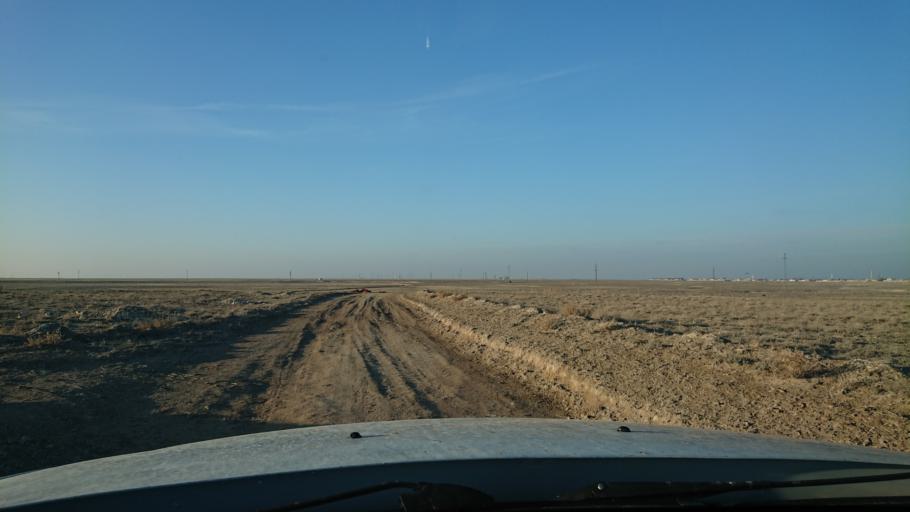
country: TR
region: Aksaray
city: Sultanhani
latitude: 38.2704
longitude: 33.5165
